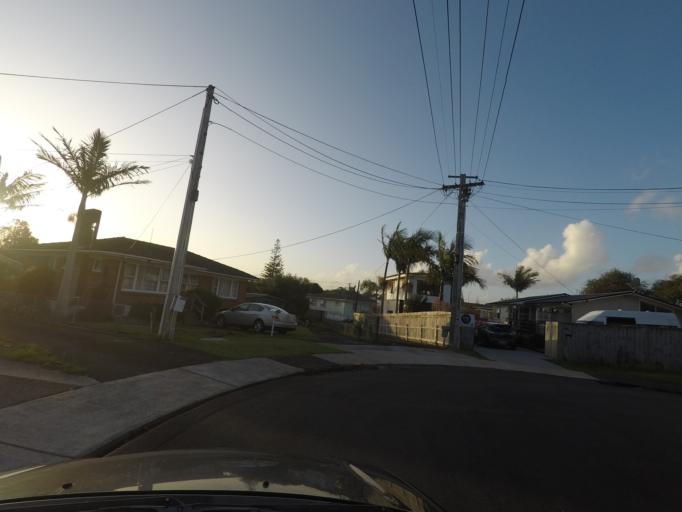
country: NZ
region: Auckland
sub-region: Auckland
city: Rosebank
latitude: -36.8481
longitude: 174.6472
